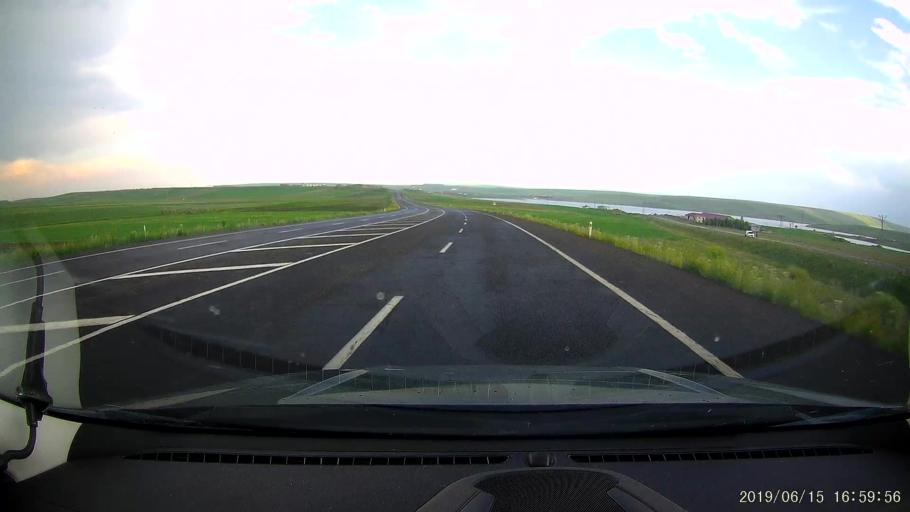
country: TR
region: Kars
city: Susuz
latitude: 40.7453
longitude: 43.1551
